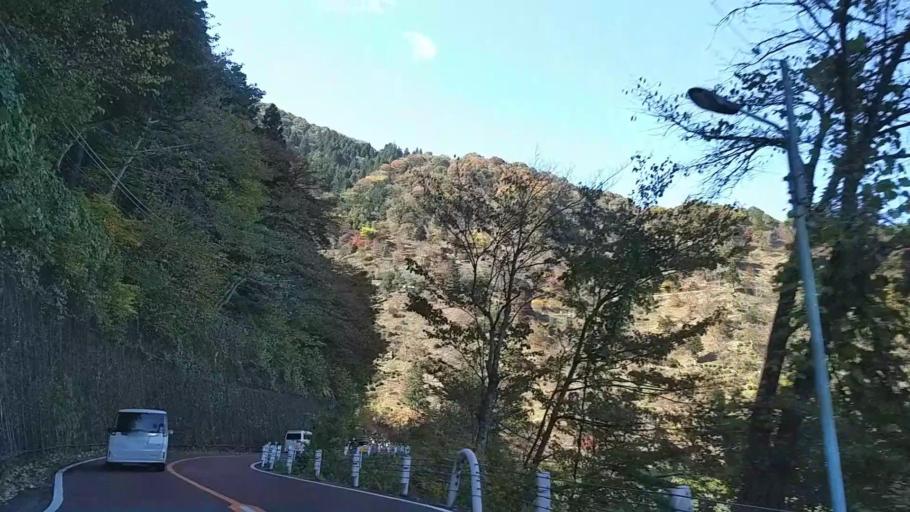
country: JP
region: Tokyo
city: Itsukaichi
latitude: 35.7883
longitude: 139.0453
